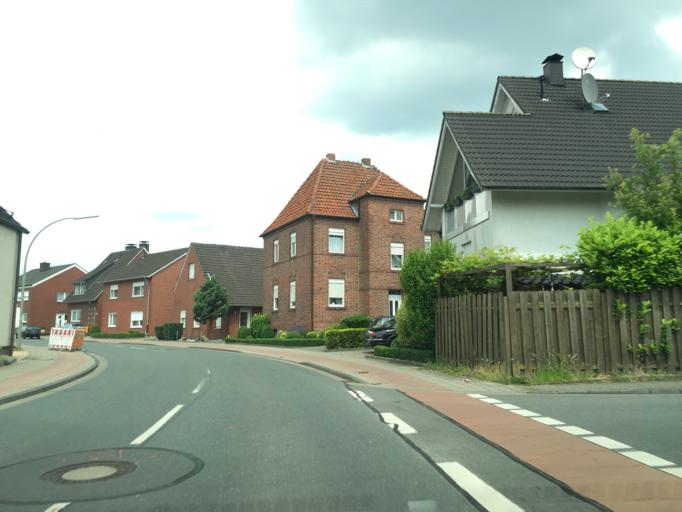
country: DE
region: North Rhine-Westphalia
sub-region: Regierungsbezirk Munster
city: Steinfurt
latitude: 52.1148
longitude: 7.3948
